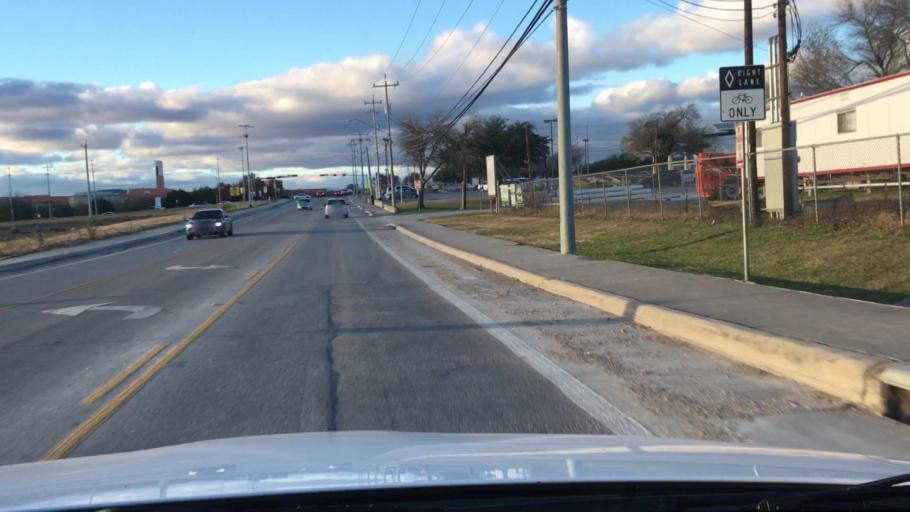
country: US
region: Texas
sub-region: Bexar County
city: Converse
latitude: 29.5421
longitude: -98.3191
